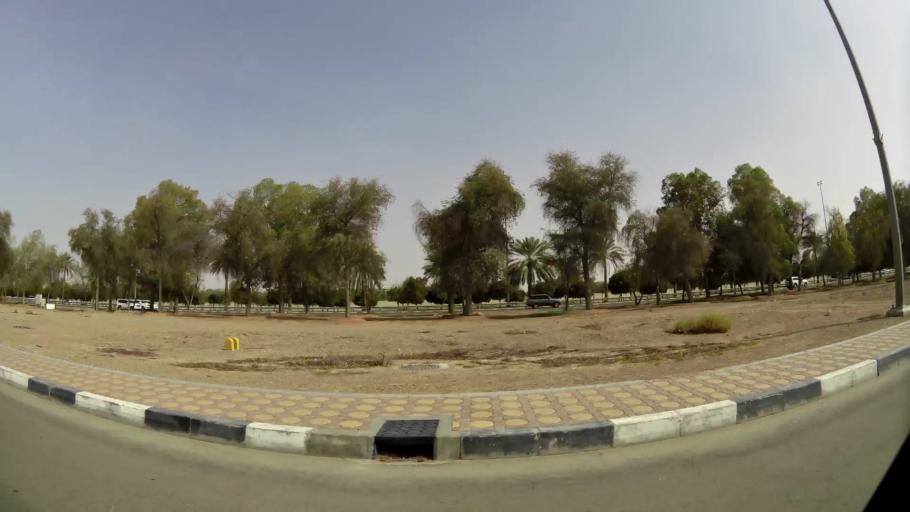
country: AE
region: Abu Dhabi
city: Al Ain
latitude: 24.1781
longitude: 55.6146
